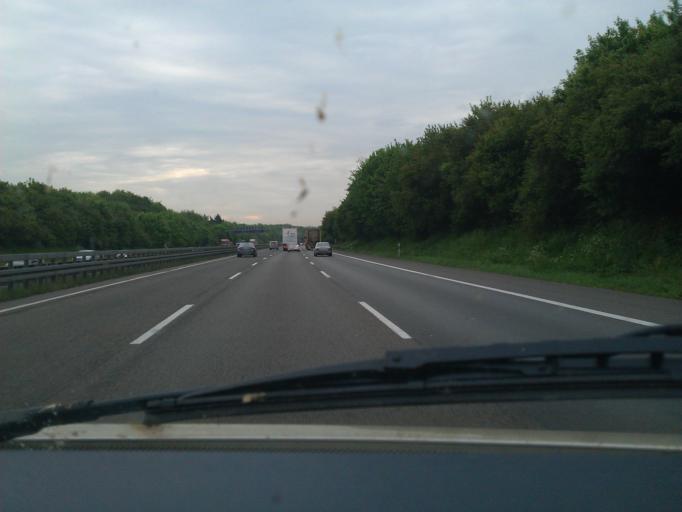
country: DE
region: North Rhine-Westphalia
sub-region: Regierungsbezirk Dusseldorf
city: Moers
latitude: 51.4935
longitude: 6.6351
